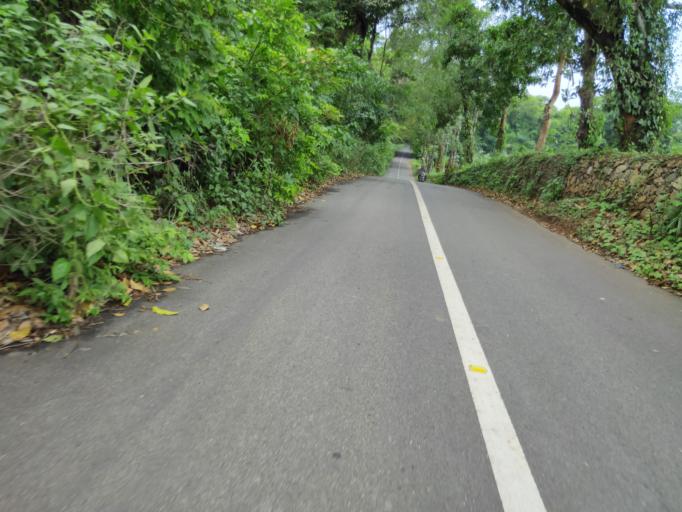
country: IN
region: Kerala
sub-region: Malappuram
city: Manjeri
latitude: 11.2253
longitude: 76.2507
